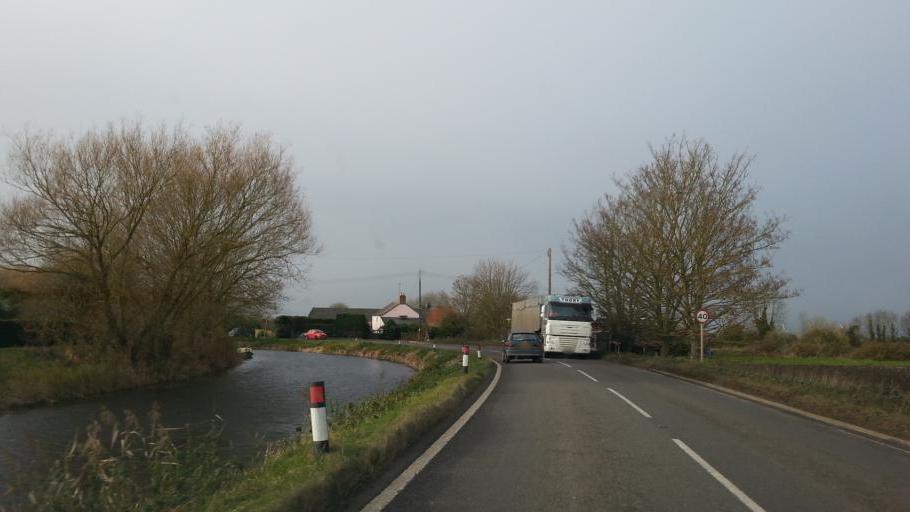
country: GB
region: England
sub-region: Norfolk
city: Outwell
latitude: 52.6047
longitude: 0.2552
